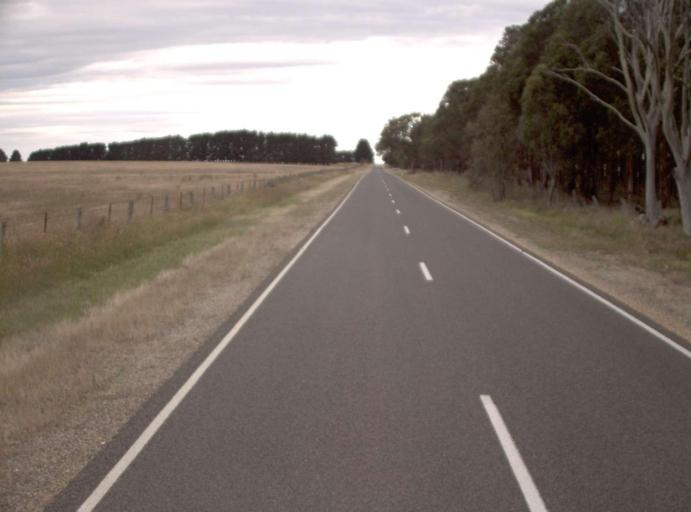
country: AU
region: Victoria
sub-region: East Gippsland
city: Bairnsdale
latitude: -37.9679
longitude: 147.4803
